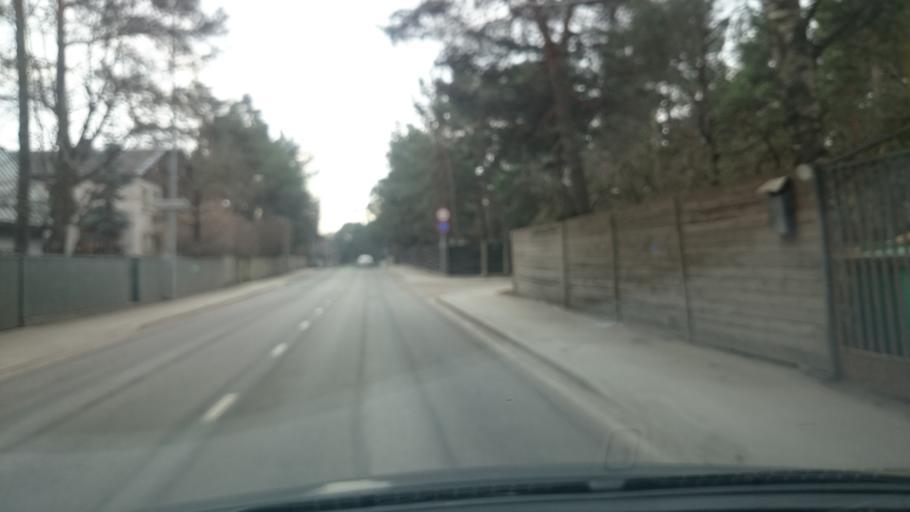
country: EE
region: Harju
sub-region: Saue vald
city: Laagri
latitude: 59.3667
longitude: 24.6299
